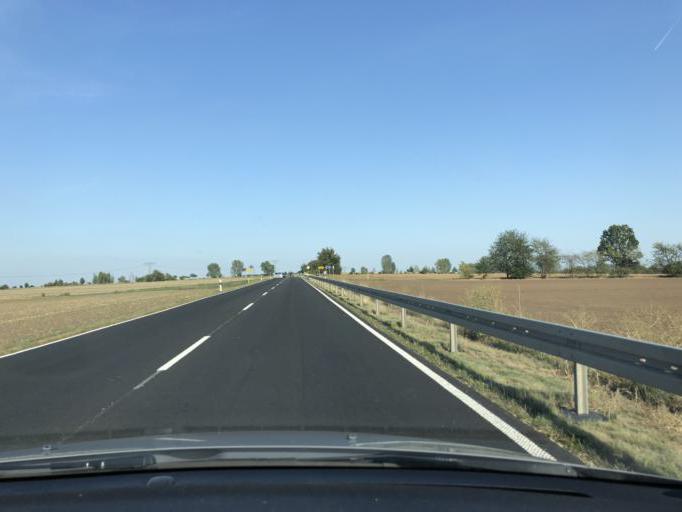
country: DE
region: Saxony-Anhalt
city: Braunsbedra
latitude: 51.2693
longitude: 11.8923
